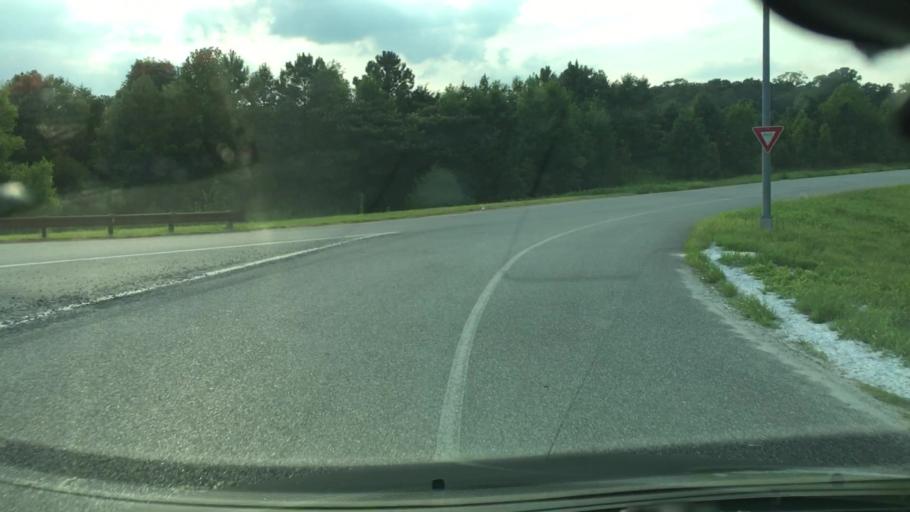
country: US
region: Maryland
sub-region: Worcester County
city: Ocean Pines
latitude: 38.3911
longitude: -75.2025
